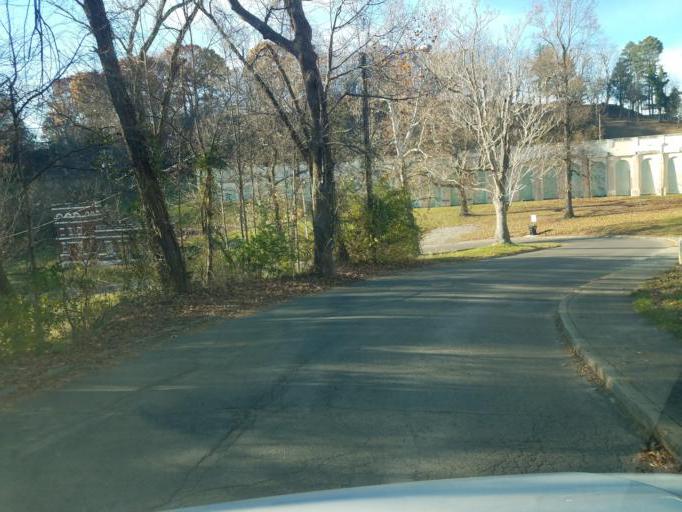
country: US
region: Ohio
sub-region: Scioto County
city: Portsmouth
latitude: 38.7531
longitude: -82.9861
